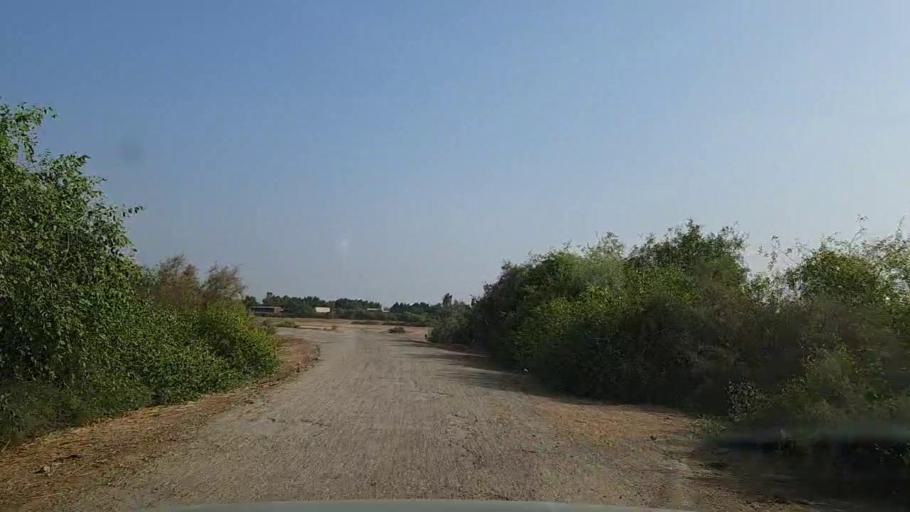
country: PK
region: Sindh
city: Mirpur Sakro
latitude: 24.5964
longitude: 67.5854
